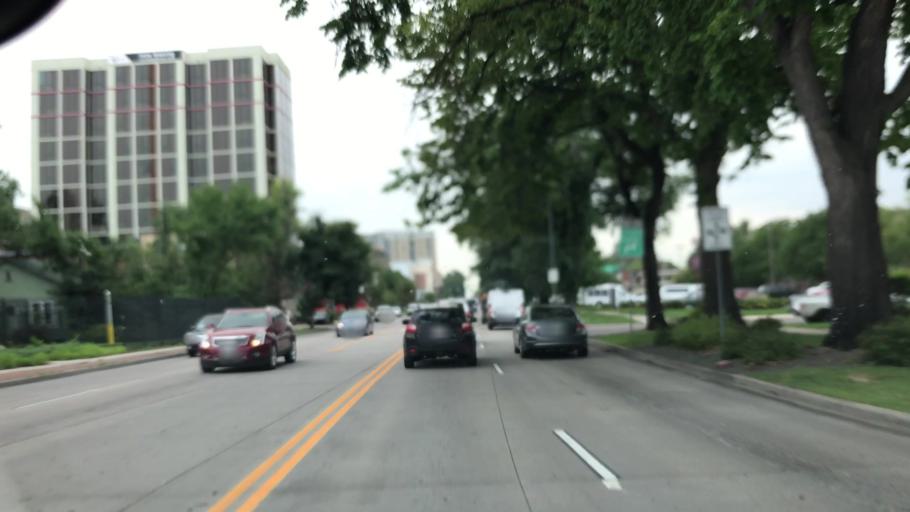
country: US
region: Colorado
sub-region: Arapahoe County
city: Glendale
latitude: 39.6824
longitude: -104.9594
